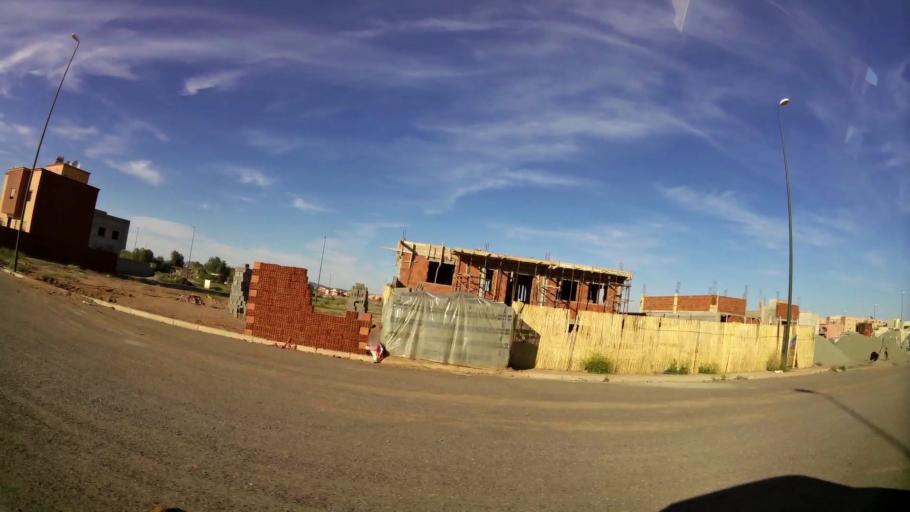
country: MA
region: Marrakech-Tensift-Al Haouz
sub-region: Marrakech
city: Marrakesh
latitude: 31.6723
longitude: -8.0713
